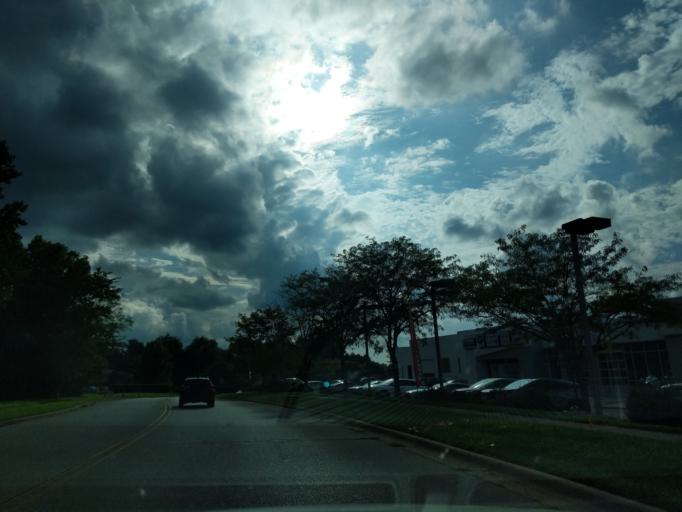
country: US
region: Kentucky
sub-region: Jefferson County
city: Hurstbourne Acres
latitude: 38.2166
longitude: -85.5790
